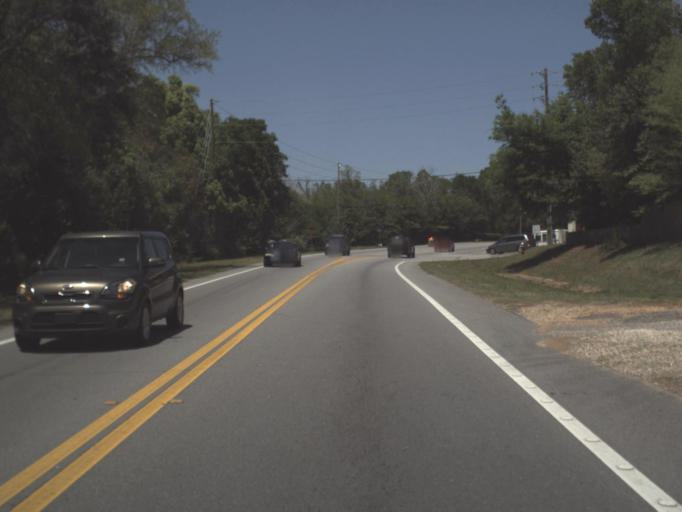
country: US
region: Florida
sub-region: Escambia County
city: Bellview
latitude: 30.4480
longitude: -87.3268
